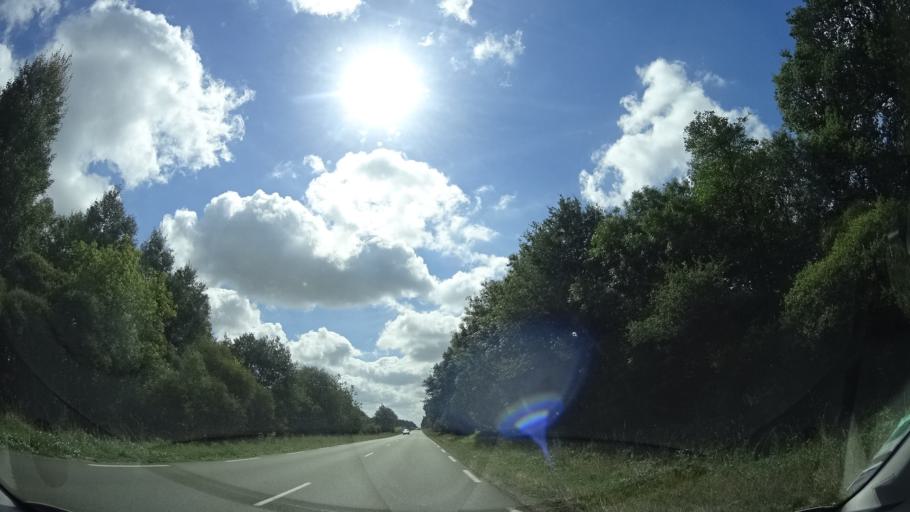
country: FR
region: Pays de la Loire
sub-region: Departement de la Mayenne
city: Meslay-du-Maine
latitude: 47.9897
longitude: -0.6262
